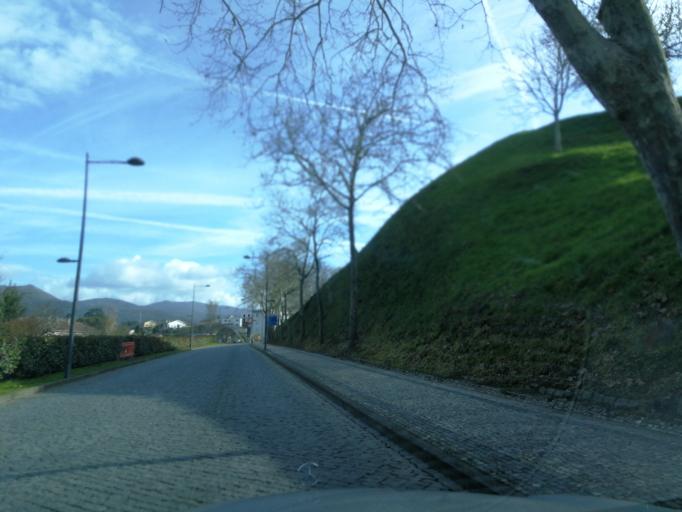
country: PT
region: Viana do Castelo
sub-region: Valenca
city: Valenca
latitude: 42.0341
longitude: -8.6441
